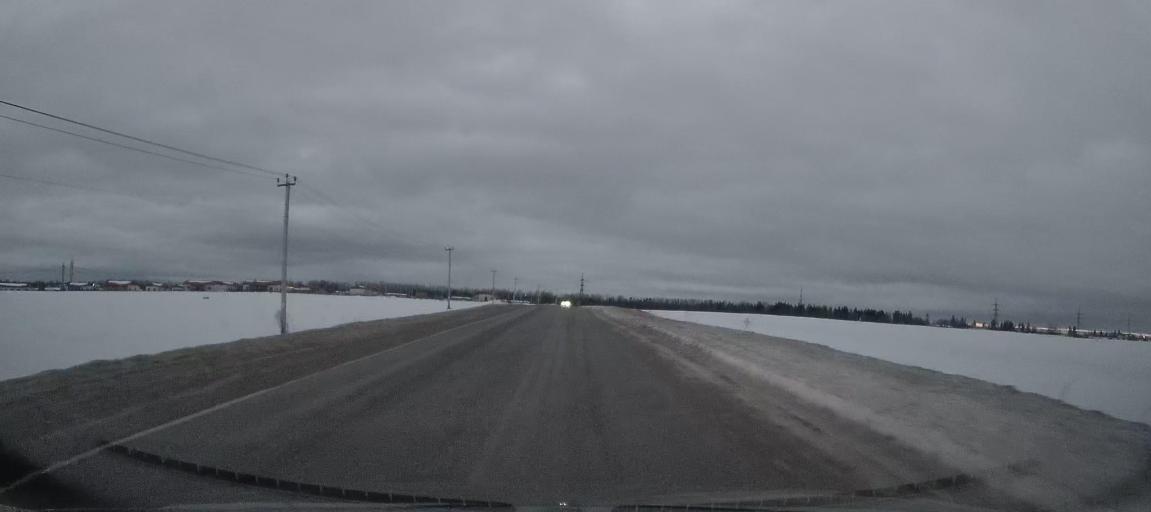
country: RU
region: Leningrad
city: Taytsy
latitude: 59.6866
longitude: 30.1221
